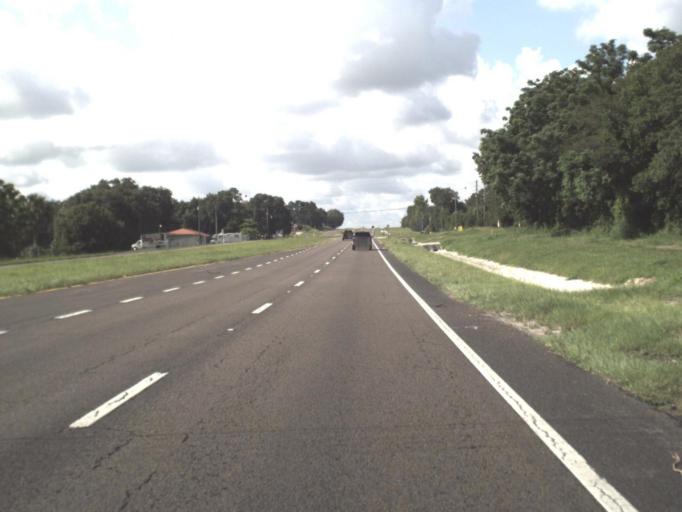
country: US
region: Florida
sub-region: Pasco County
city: Zephyrhills North
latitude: 28.2903
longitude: -82.1879
